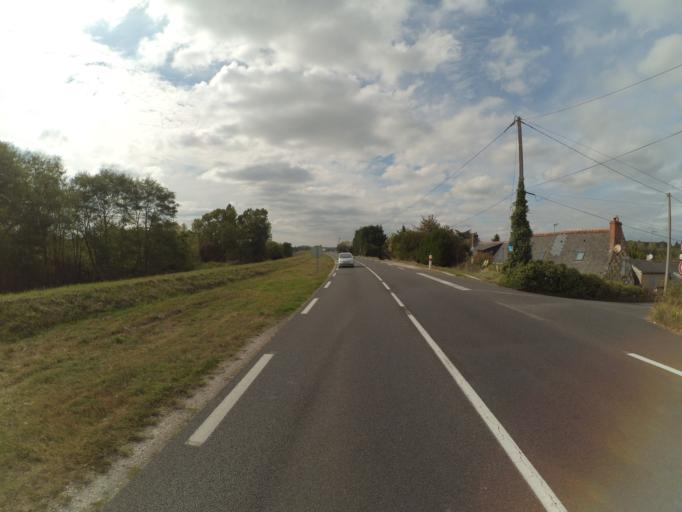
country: FR
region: Centre
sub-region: Departement d'Indre-et-Loire
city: Fondettes
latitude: 47.3844
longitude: 0.5903
